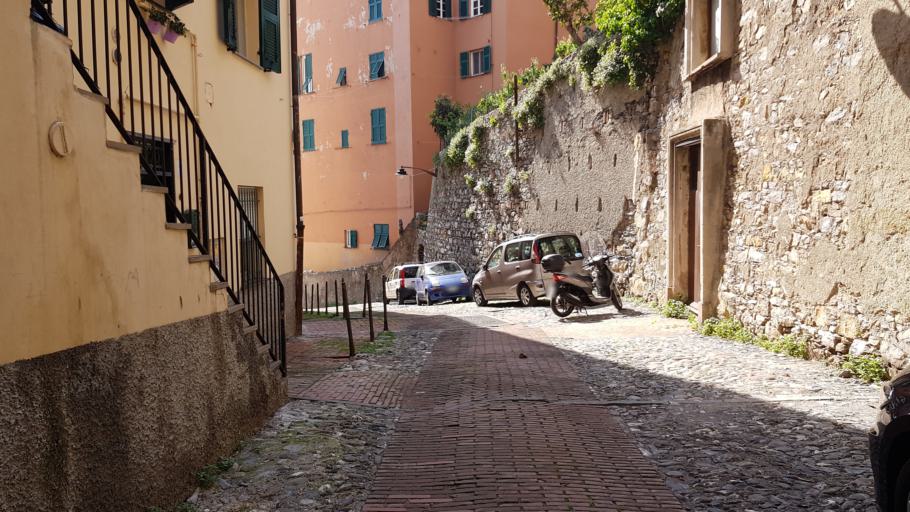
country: IT
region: Liguria
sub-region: Provincia di Genova
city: Genoa
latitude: 44.4170
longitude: 8.9252
